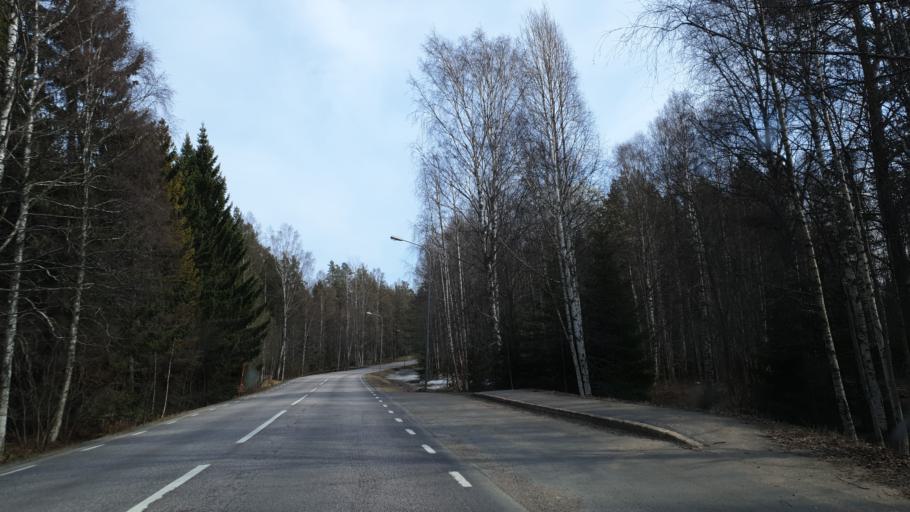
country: SE
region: Gaevleborg
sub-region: Gavle Kommun
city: Norrsundet
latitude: 60.9994
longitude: 17.0988
